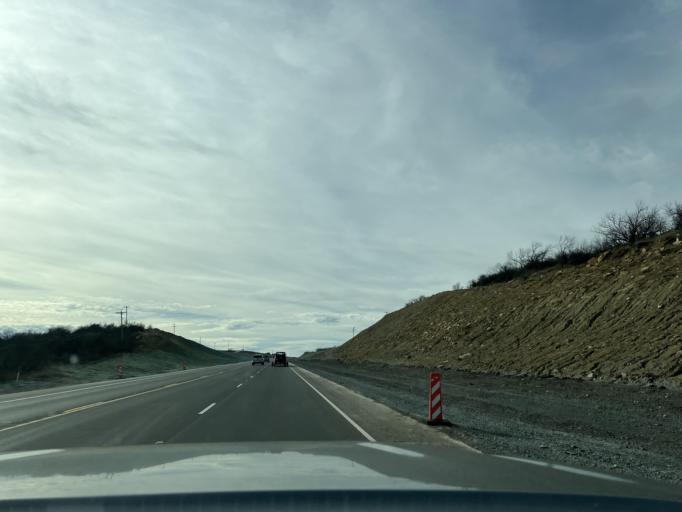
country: US
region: Texas
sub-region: Shackelford County
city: Albany
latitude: 32.7084
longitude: -99.3737
